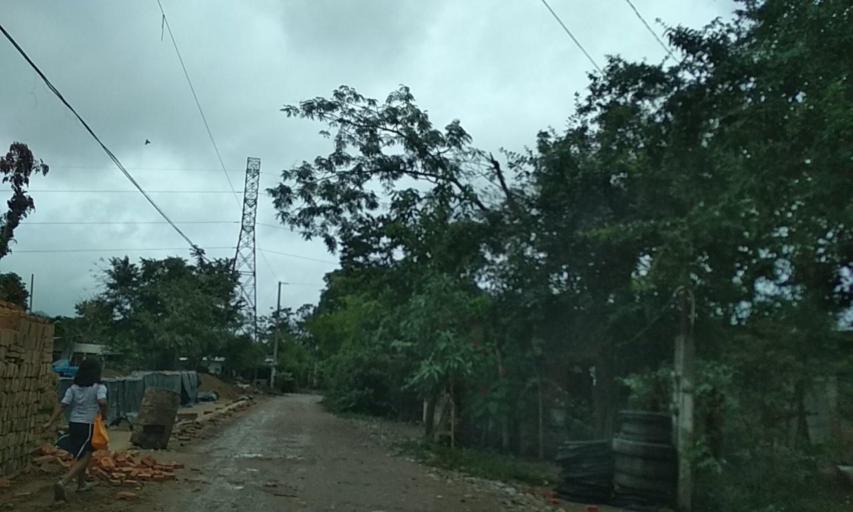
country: MX
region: Veracruz
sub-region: Papantla
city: El Chote
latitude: 20.3742
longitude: -97.3331
